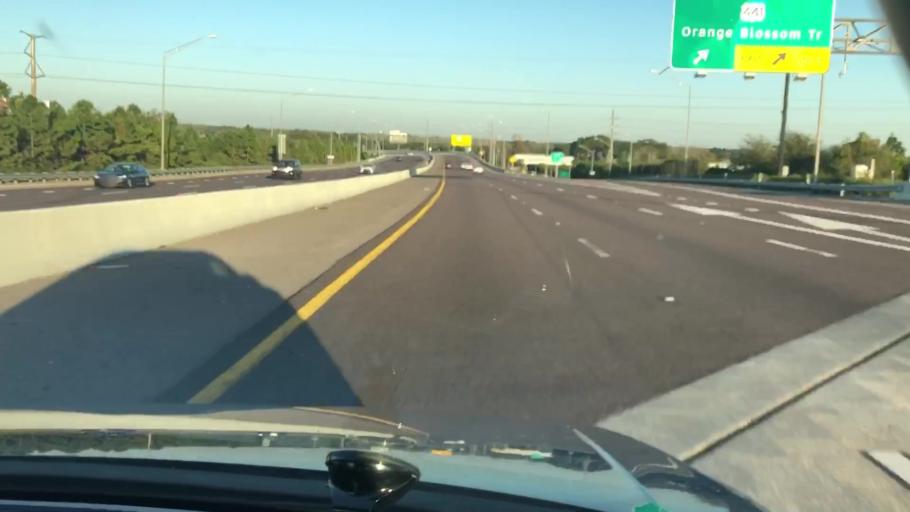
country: US
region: Florida
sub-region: Orange County
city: Lockhart
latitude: 28.6334
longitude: -81.4568
